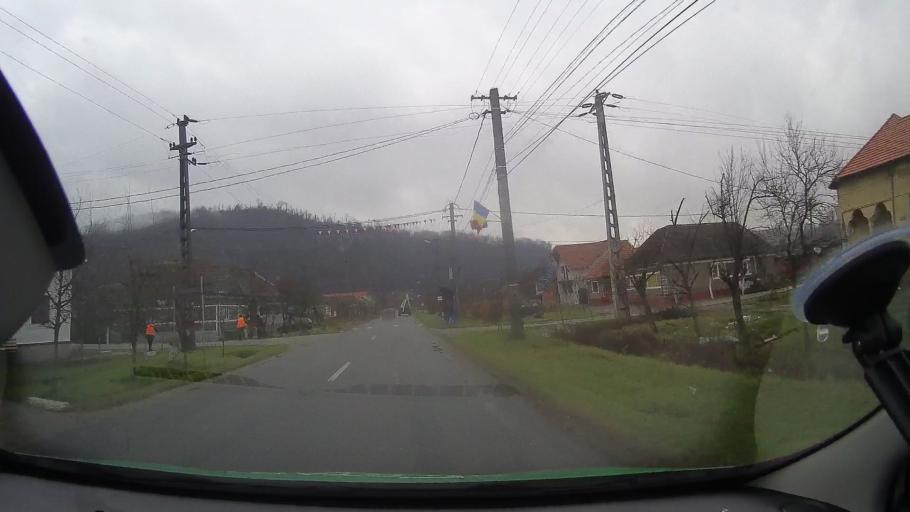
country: RO
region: Arad
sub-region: Comuna Ignesti
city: Ignesti
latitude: 46.3781
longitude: 22.1455
